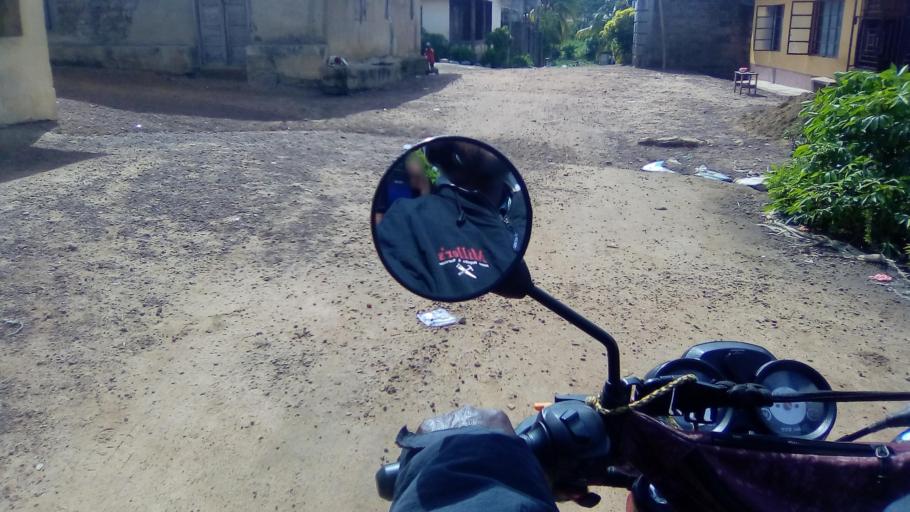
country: SL
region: Southern Province
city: Bo
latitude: 7.9551
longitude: -11.7477
